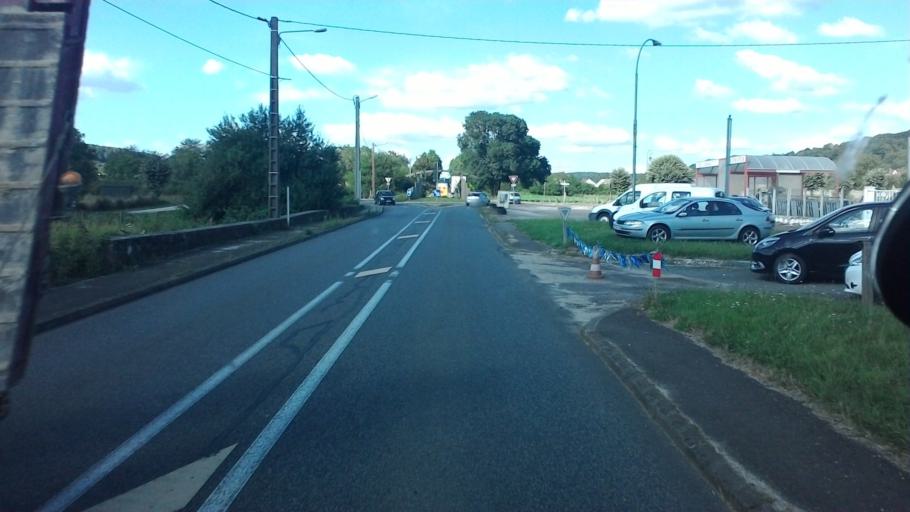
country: FR
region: Franche-Comte
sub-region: Departement de la Haute-Saone
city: Vaivre-et-Montoille
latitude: 47.5393
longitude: 6.0478
